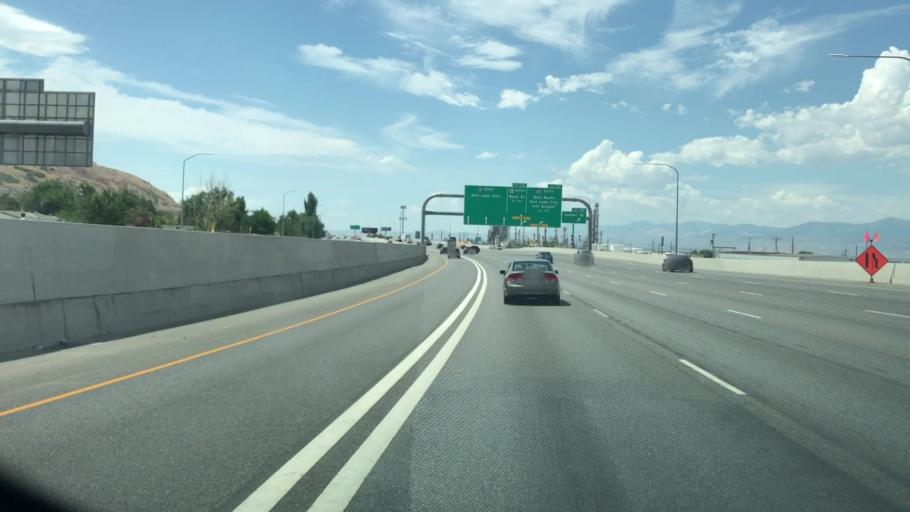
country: US
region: Utah
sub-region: Davis County
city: North Salt Lake
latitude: 40.8467
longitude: -111.9140
